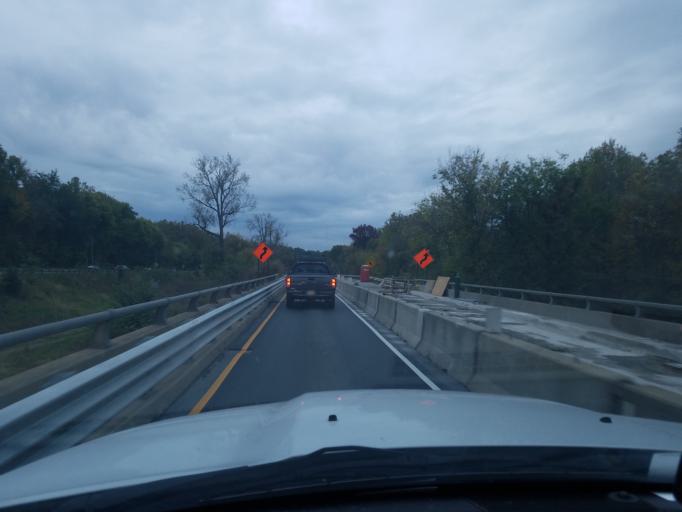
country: US
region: Kentucky
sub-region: Henderson County
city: Henderson
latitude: 37.8977
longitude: -87.5538
